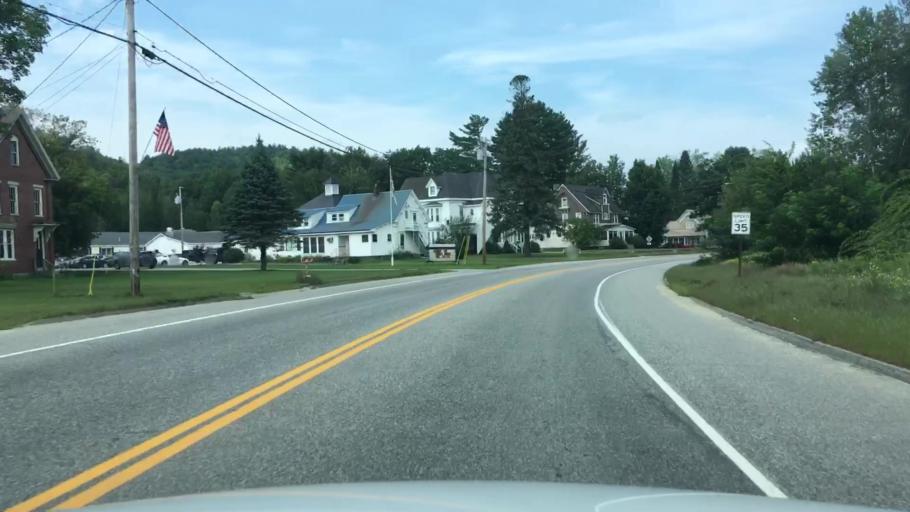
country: US
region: Maine
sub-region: Oxford County
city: Canton
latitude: 44.4411
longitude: -70.3161
